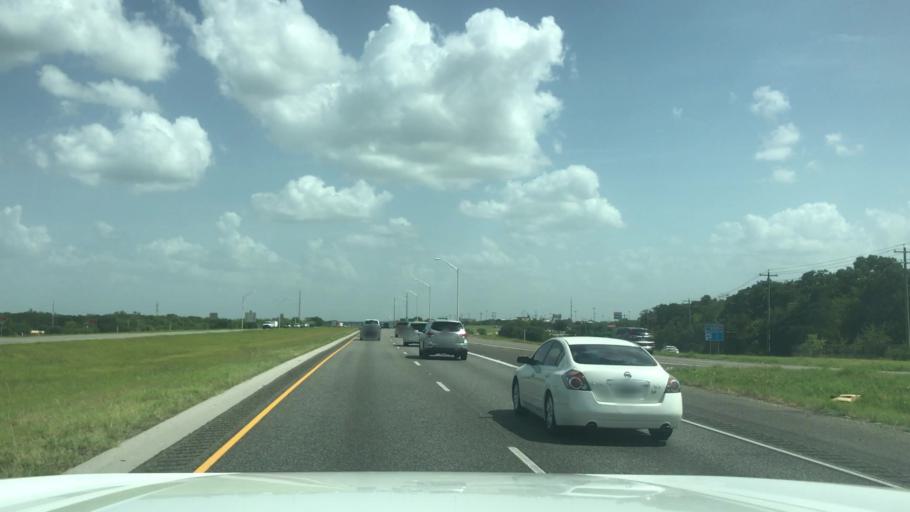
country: US
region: Texas
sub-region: Brazos County
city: College Station
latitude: 30.6342
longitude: -96.3052
